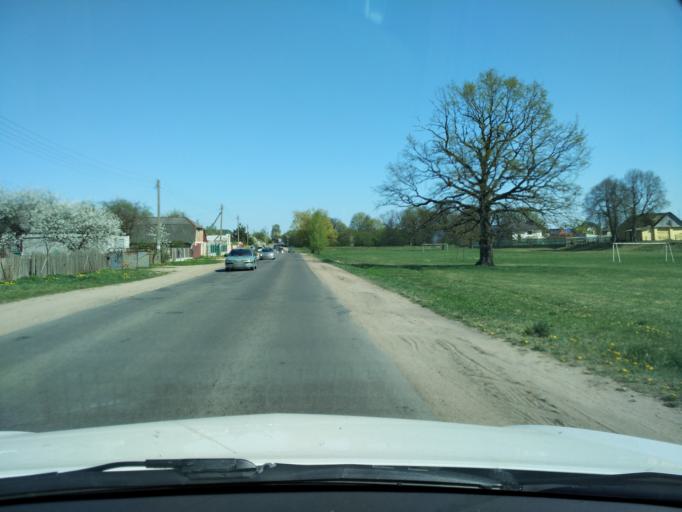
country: BY
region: Minsk
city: Lyeskawka
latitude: 54.0019
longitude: 27.7111
